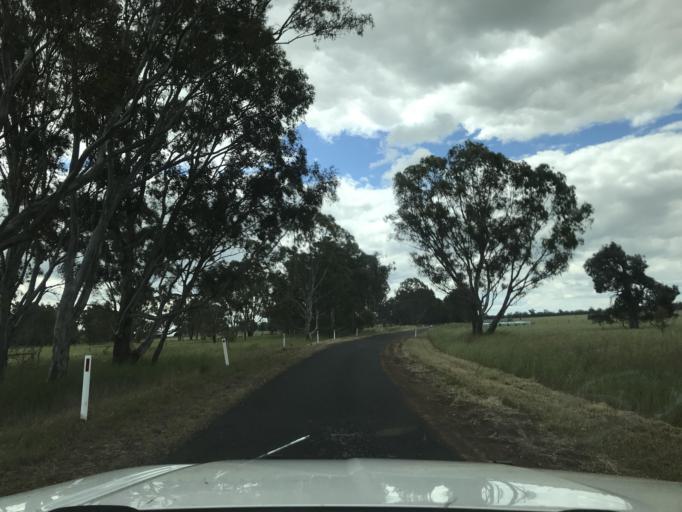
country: AU
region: South Australia
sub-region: Naracoorte and Lucindale
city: Naracoorte
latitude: -37.0720
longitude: 141.1718
